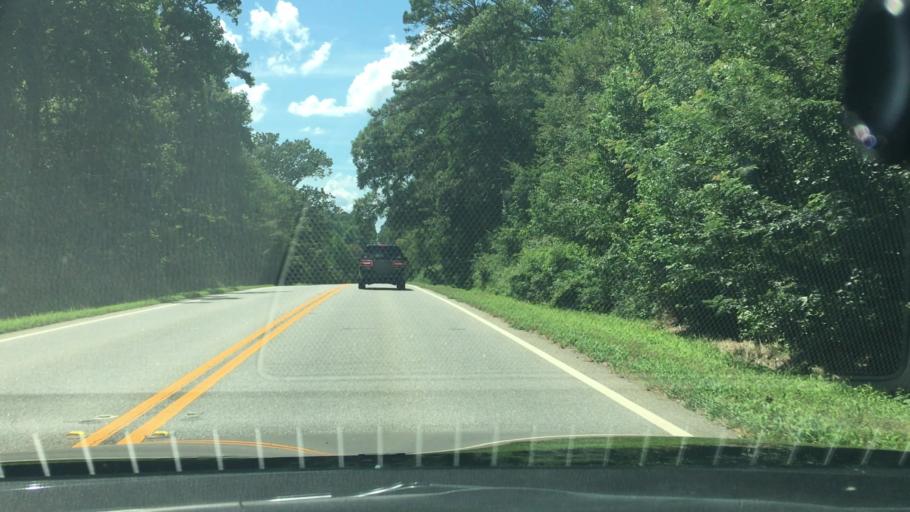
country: US
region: Georgia
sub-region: Putnam County
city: Eatonton
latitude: 33.3091
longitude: -83.5085
